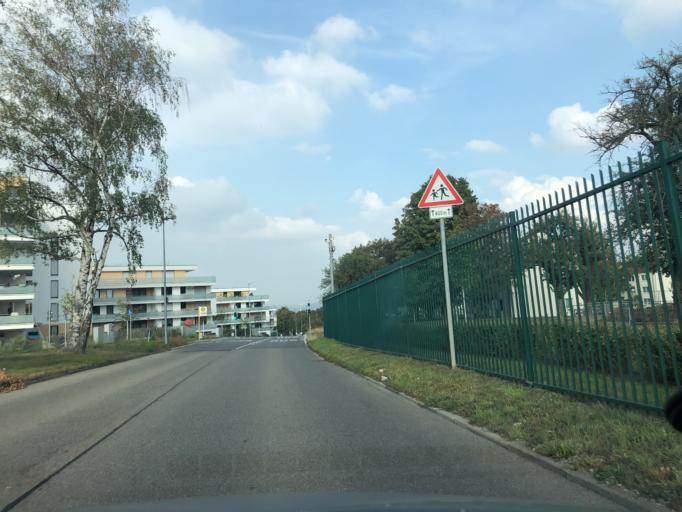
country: DE
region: Baden-Wuerttemberg
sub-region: Regierungsbezirk Stuttgart
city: Stuttgart Feuerbach
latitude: 48.8245
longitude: 9.1880
